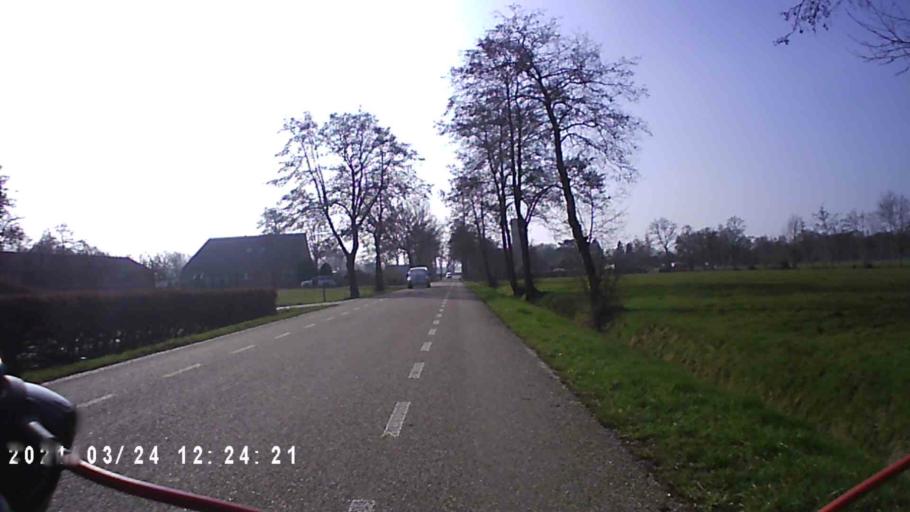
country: NL
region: Groningen
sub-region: Gemeente Leek
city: Leek
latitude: 53.1835
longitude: 6.3929
